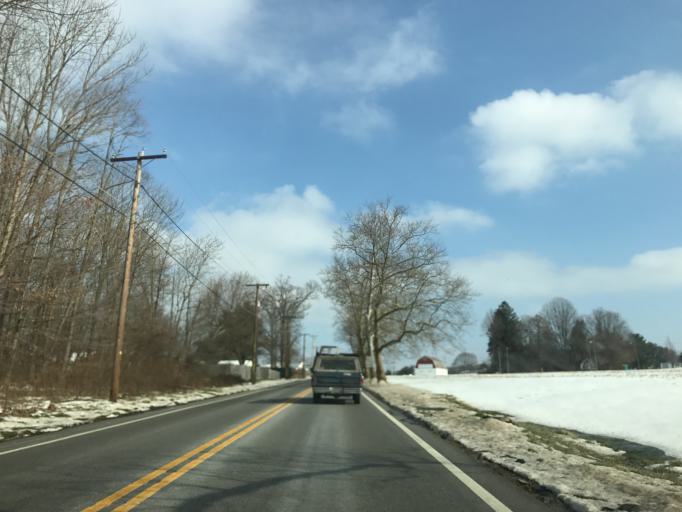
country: US
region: Maryland
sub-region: Harford County
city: South Bel Air
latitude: 39.6529
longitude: -76.2696
